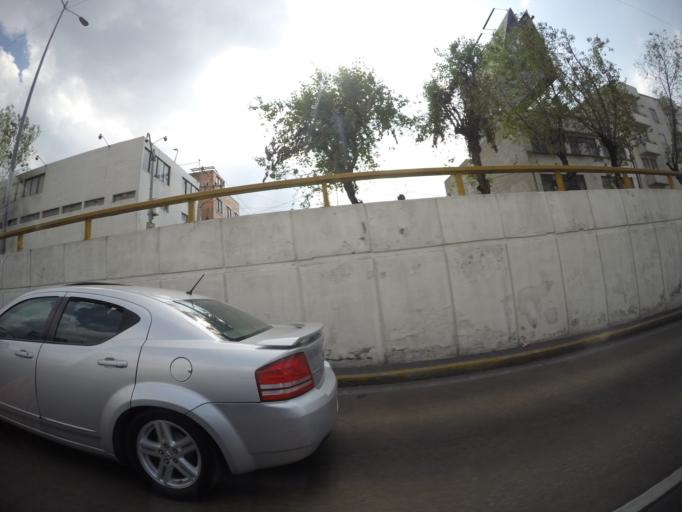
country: MX
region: Mexico City
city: Cuauhtemoc
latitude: 19.4604
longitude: -99.1256
